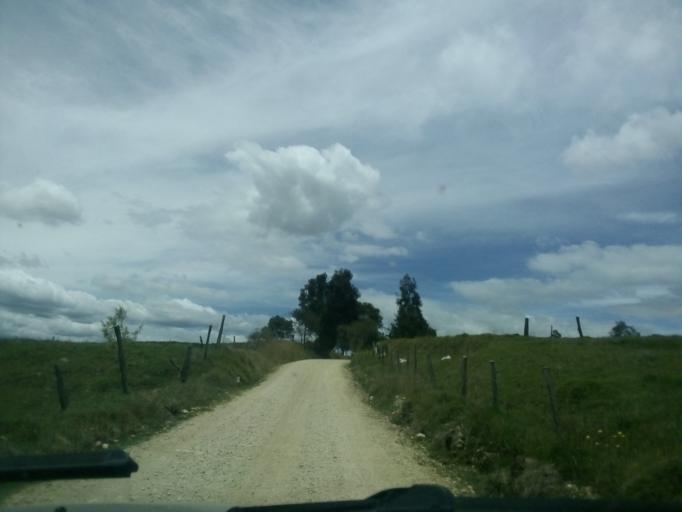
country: CO
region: Boyaca
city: Toca
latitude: 5.5981
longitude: -73.1575
